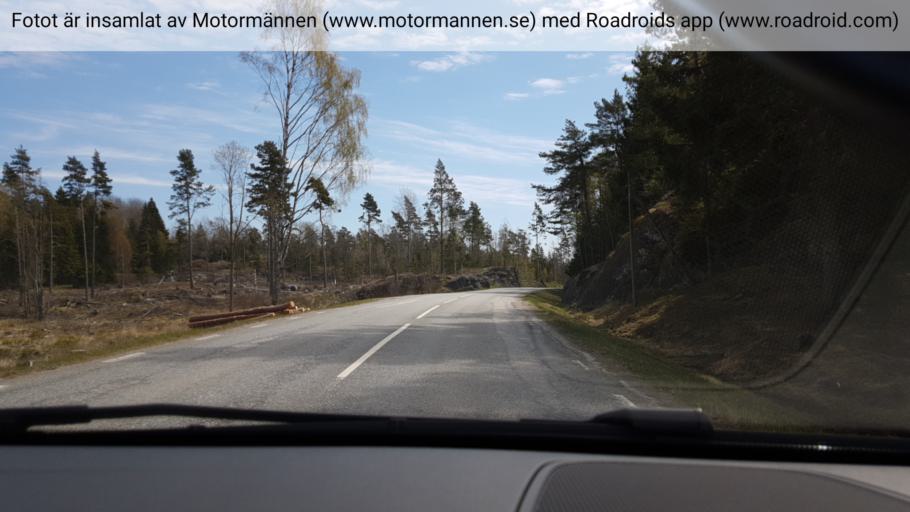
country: SE
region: Stockholm
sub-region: Nynashamns Kommun
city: Osmo
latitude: 58.9711
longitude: 17.9376
